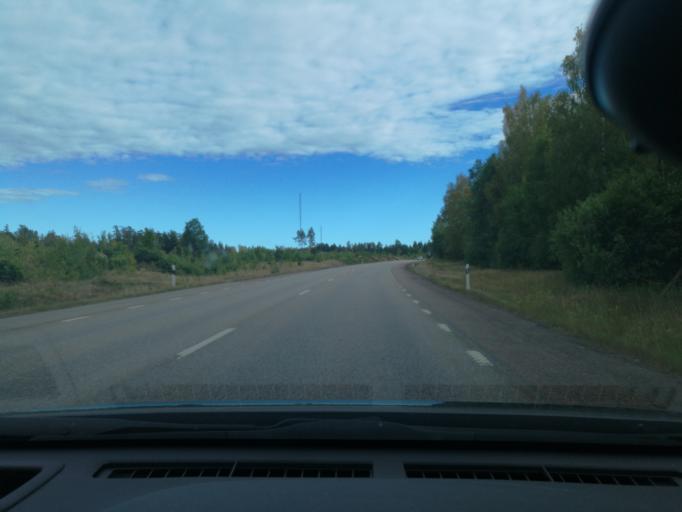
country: SE
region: Kalmar
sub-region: Oskarshamns Kommun
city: Oskarshamn
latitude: 57.4902
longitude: 16.5177
